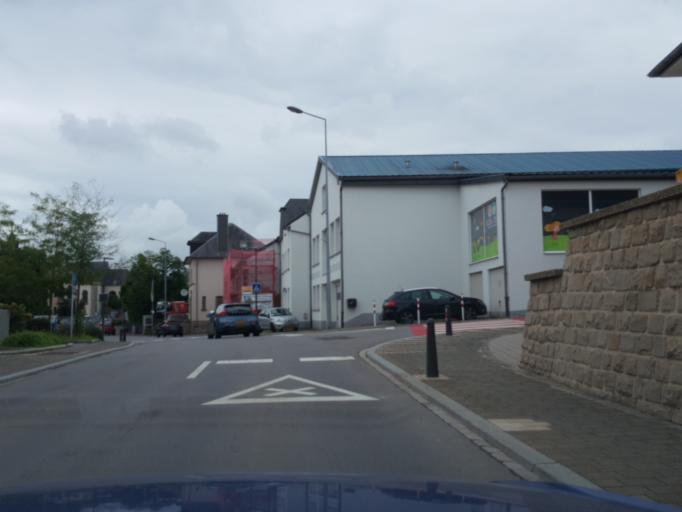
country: LU
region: Luxembourg
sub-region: Canton de Capellen
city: Mamer
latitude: 49.6279
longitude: 6.0211
